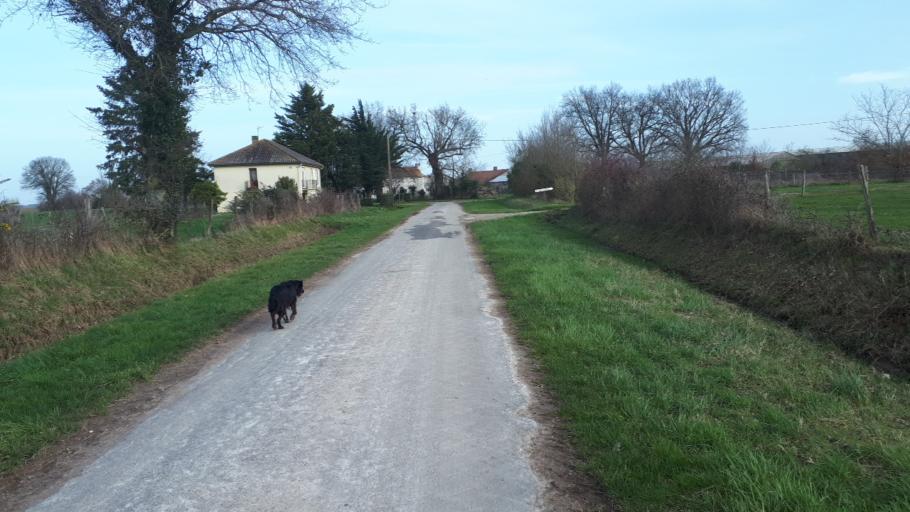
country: FR
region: Poitou-Charentes
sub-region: Departement de la Vienne
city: Archigny
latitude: 46.6201
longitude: 0.7508
